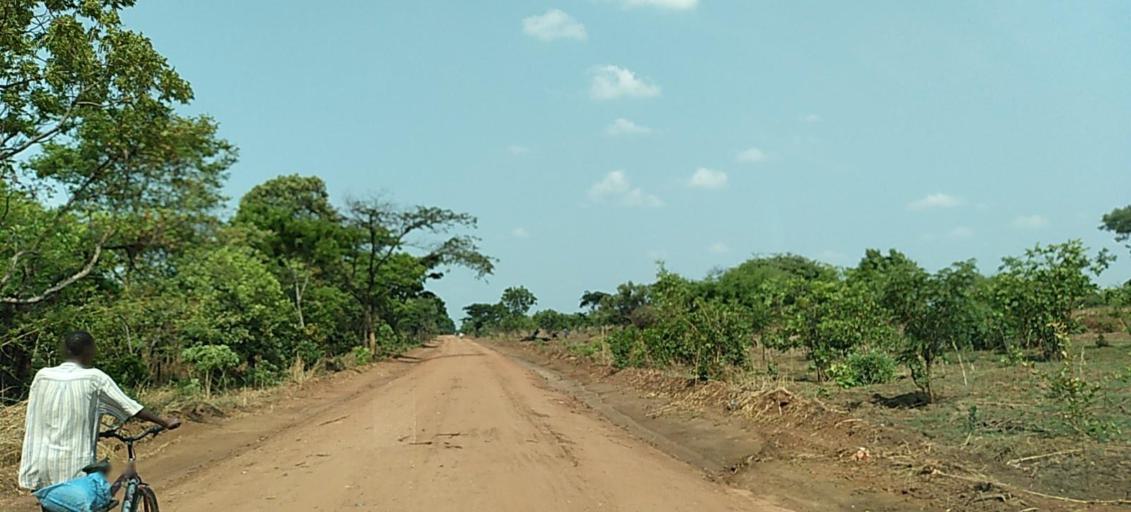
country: ZM
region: Copperbelt
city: Luanshya
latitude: -13.0909
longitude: 28.2844
